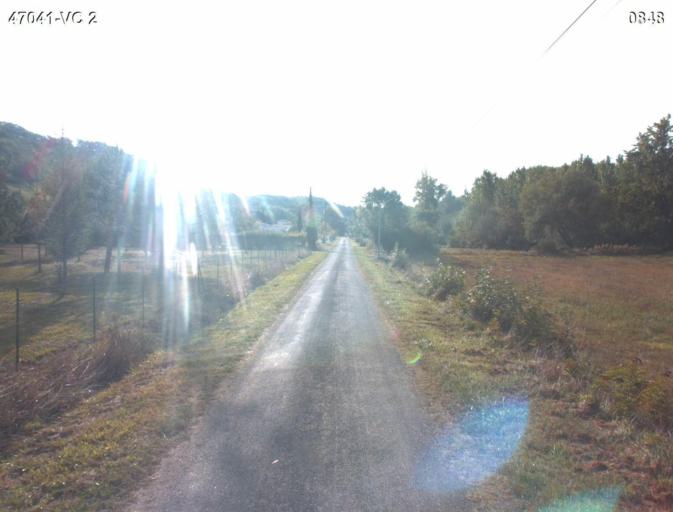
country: FR
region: Aquitaine
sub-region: Departement du Lot-et-Garonne
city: Port-Sainte-Marie
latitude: 44.1948
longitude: 0.4122
